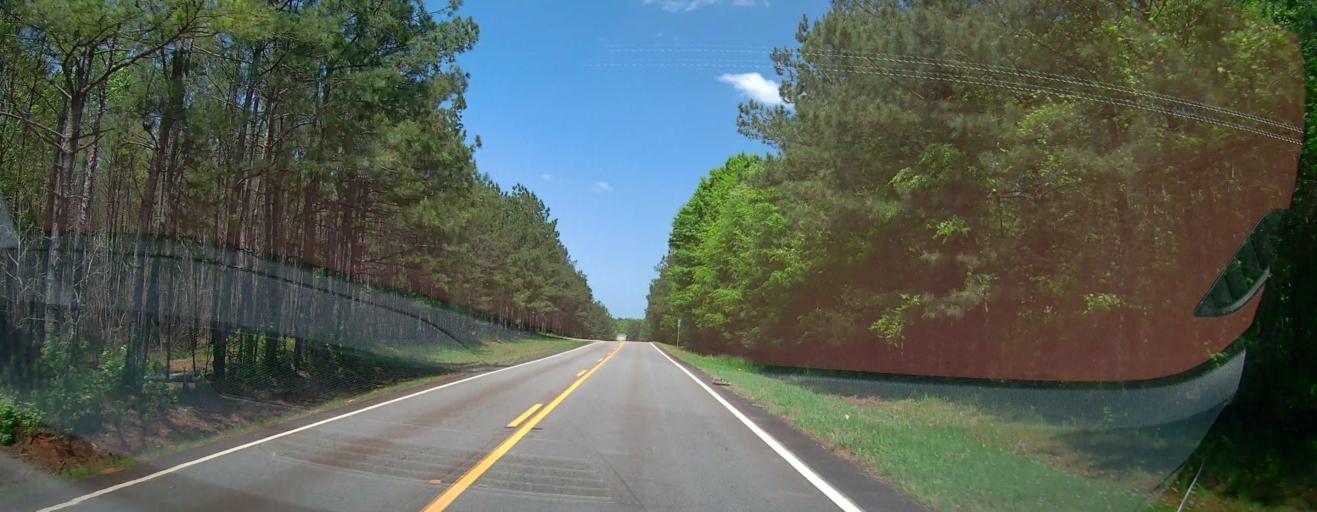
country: US
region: Georgia
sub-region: Jones County
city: Gray
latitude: 33.1284
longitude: -83.6295
